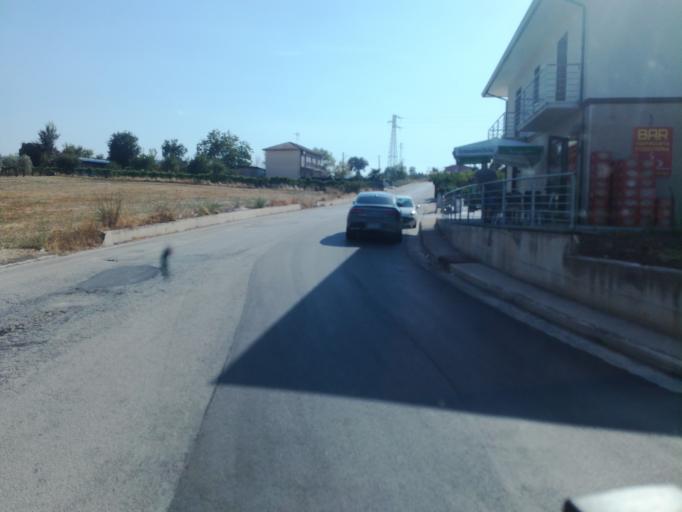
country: IT
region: Campania
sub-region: Provincia di Avellino
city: Grottaminarda
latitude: 41.0651
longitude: 15.0730
